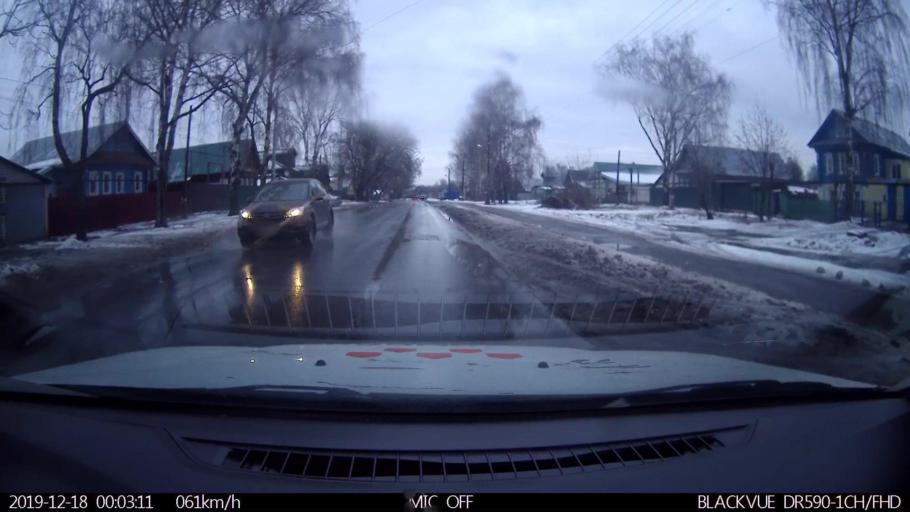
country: RU
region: Nizjnij Novgorod
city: Gorbatovka
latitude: 56.3671
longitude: 43.8346
